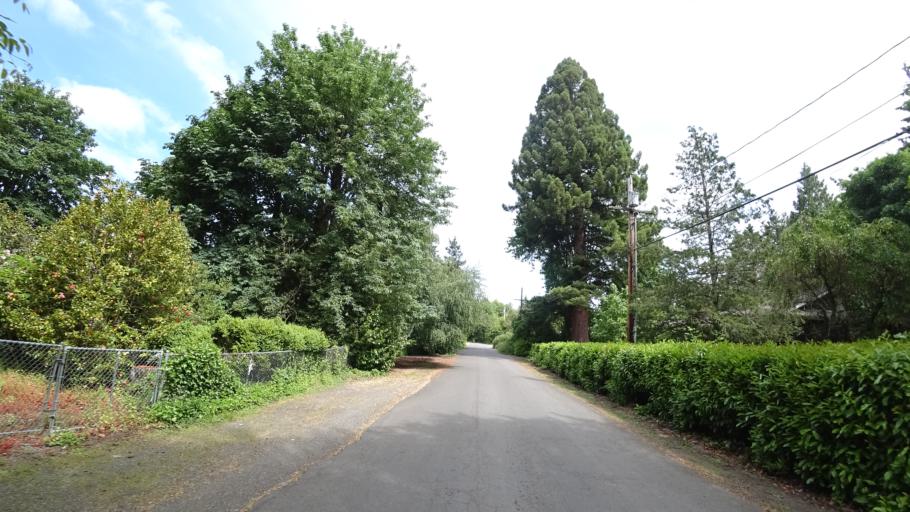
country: US
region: Oregon
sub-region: Clackamas County
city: Lake Oswego
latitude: 45.4490
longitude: -122.6834
